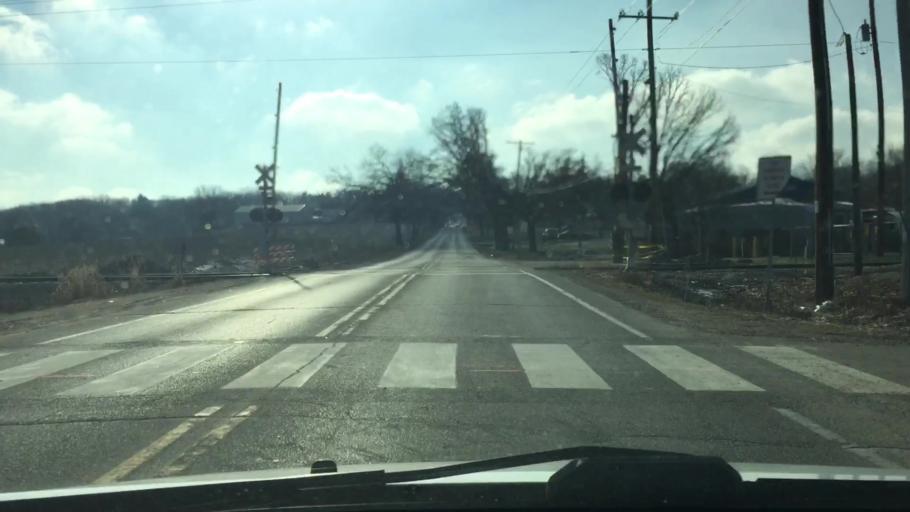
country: US
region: Wisconsin
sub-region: Waukesha County
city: Waukesha
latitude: 42.9932
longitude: -88.2896
